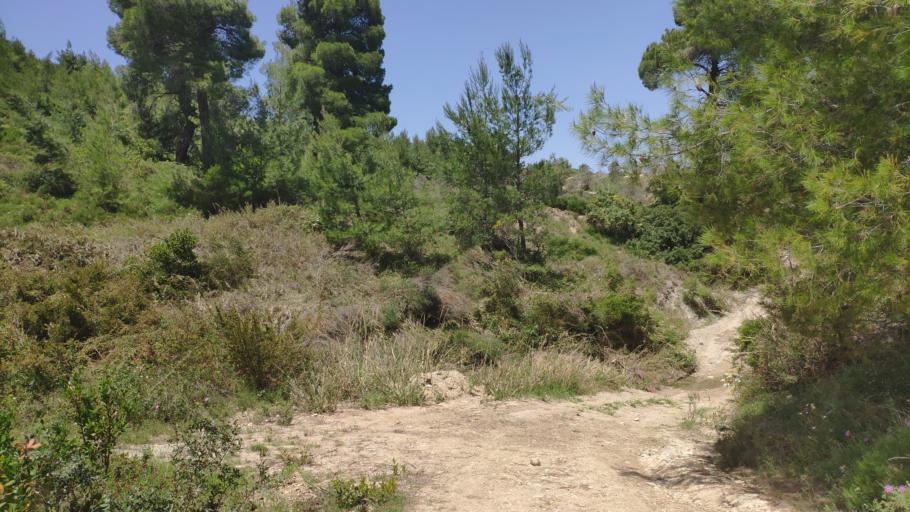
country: GR
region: Attica
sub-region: Nomarchia Anatolikis Attikis
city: Kalamos
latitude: 38.2770
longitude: 23.8472
